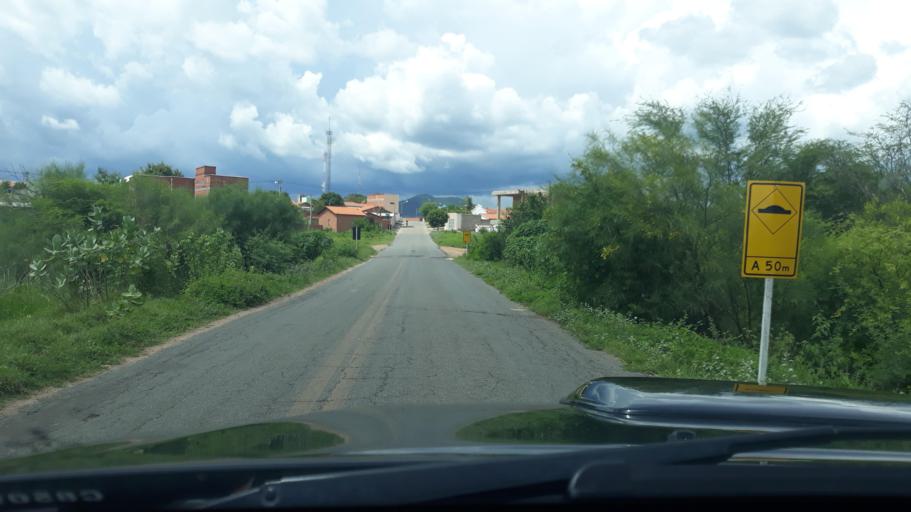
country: BR
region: Bahia
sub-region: Guanambi
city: Guanambi
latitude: -13.9129
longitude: -42.8436
